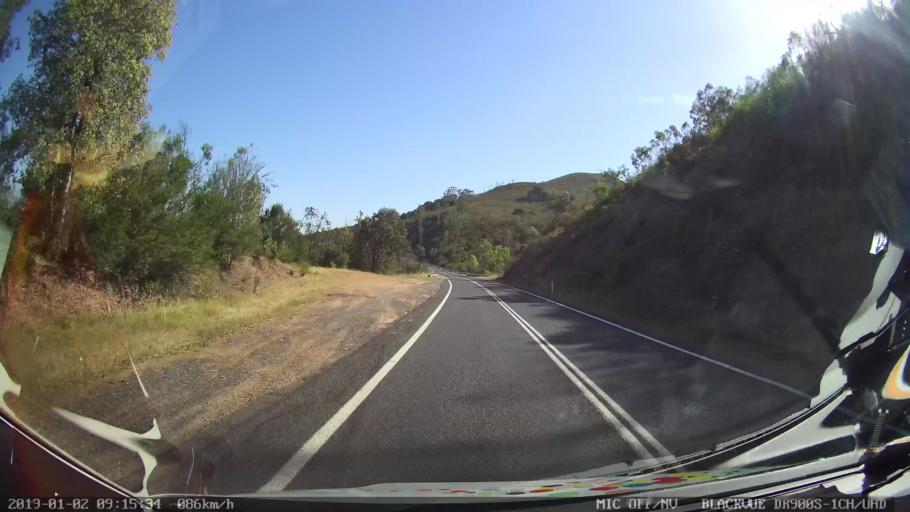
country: AU
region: New South Wales
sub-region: Tumut Shire
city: Tumut
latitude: -35.4636
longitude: 148.2804
